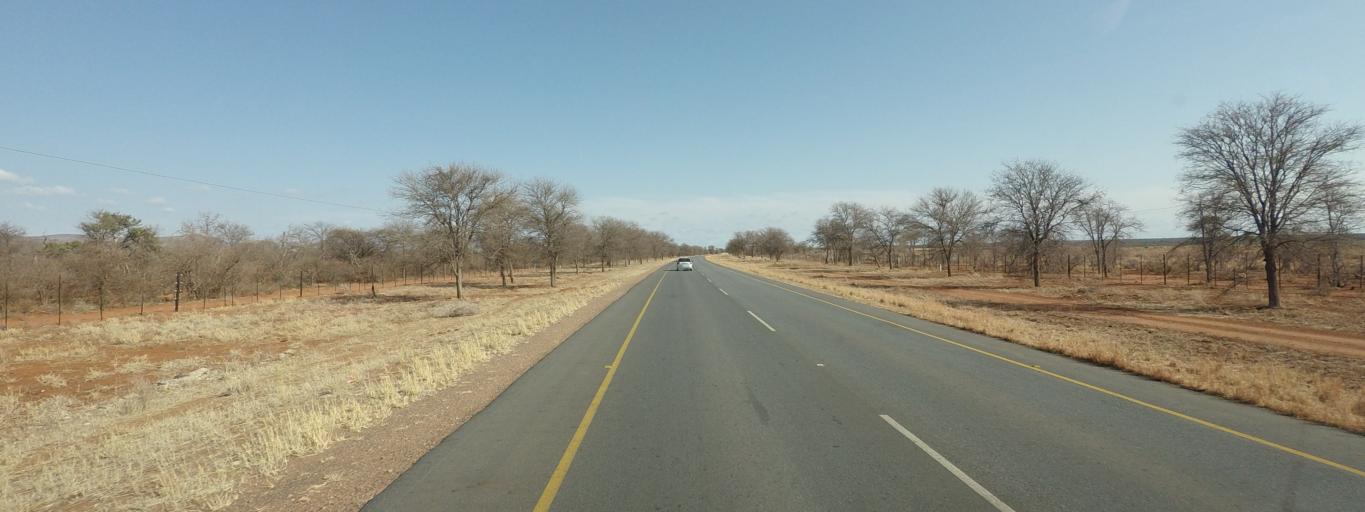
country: BW
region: Central
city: Makobeng
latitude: -22.9785
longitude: 27.9176
